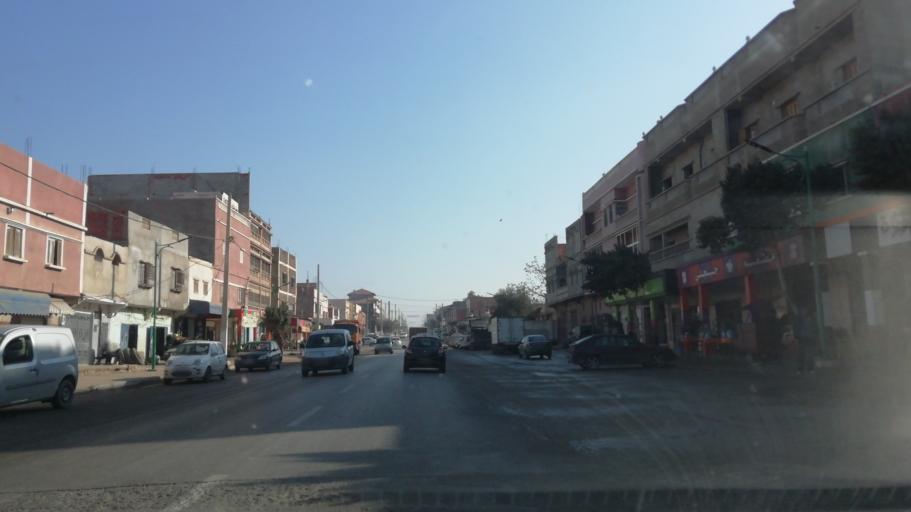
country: DZ
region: Relizane
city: Relizane
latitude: 35.7332
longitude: 0.4556
